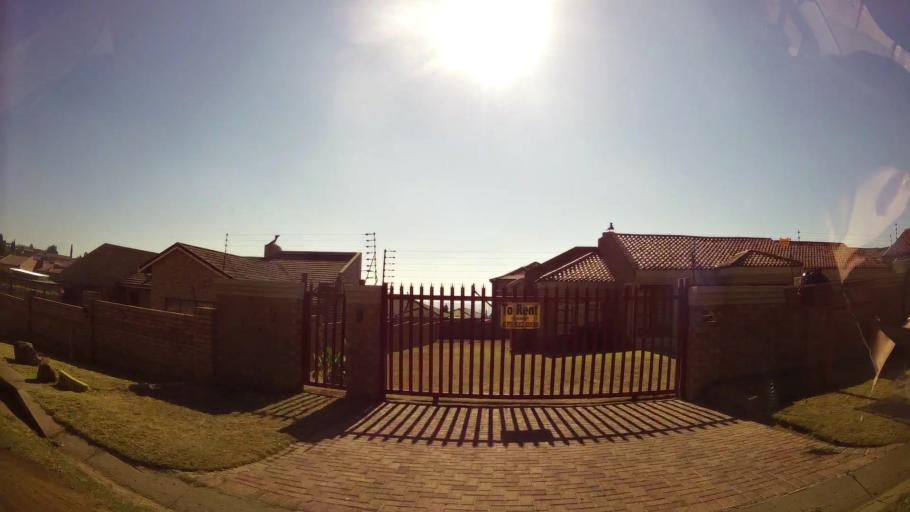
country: ZA
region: Mpumalanga
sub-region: Nkangala District Municipality
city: Witbank
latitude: -25.8622
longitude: 29.2433
